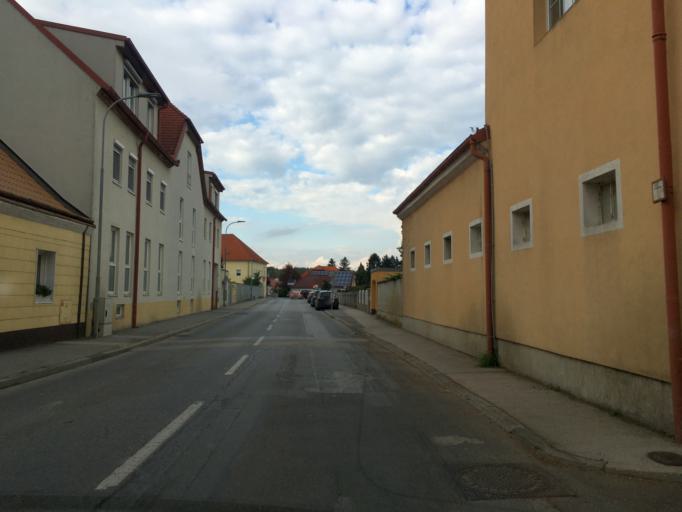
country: AT
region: Lower Austria
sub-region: Politischer Bezirk Wien-Umgebung
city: Fischamend Dorf
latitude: 48.1191
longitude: 16.6066
